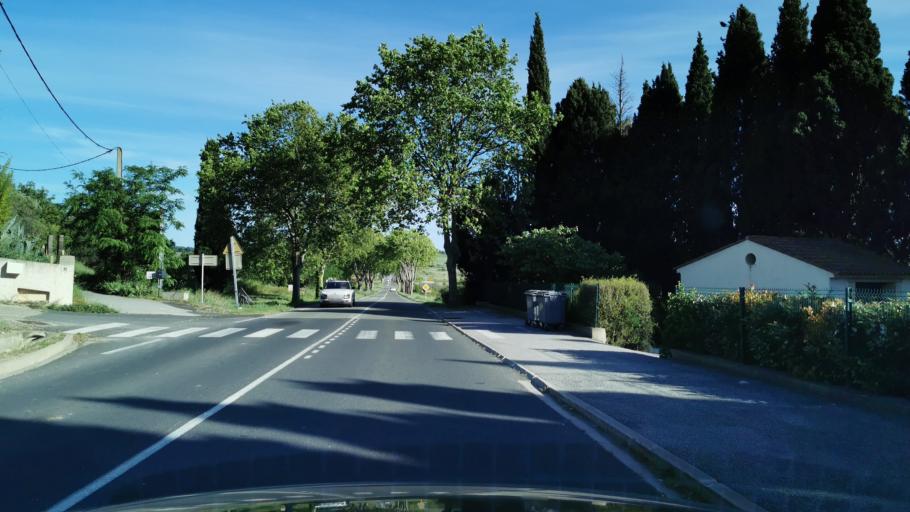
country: FR
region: Languedoc-Roussillon
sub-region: Departement de l'Aude
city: Marcorignan
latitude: 43.2224
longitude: 2.9244
